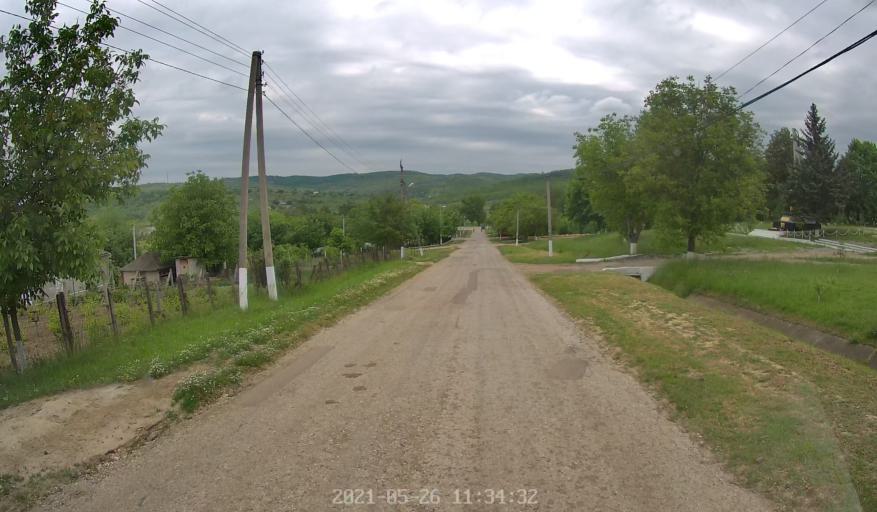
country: MD
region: Hincesti
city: Dancu
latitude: 46.8260
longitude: 28.3658
